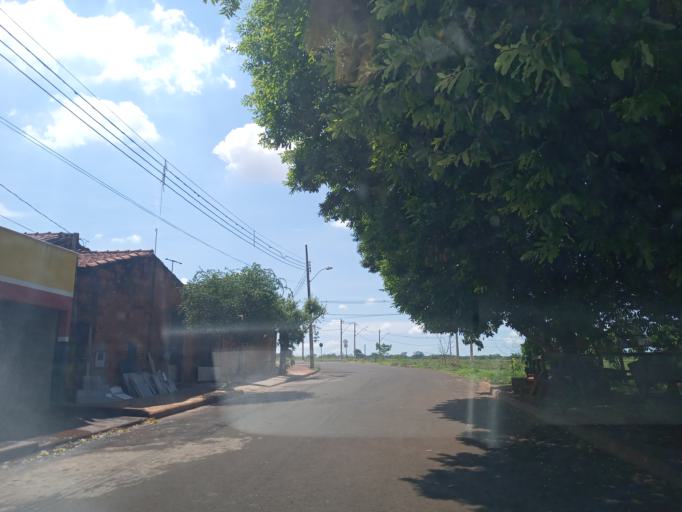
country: BR
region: Minas Gerais
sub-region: Ituiutaba
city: Ituiutaba
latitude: -18.9988
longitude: -49.4756
